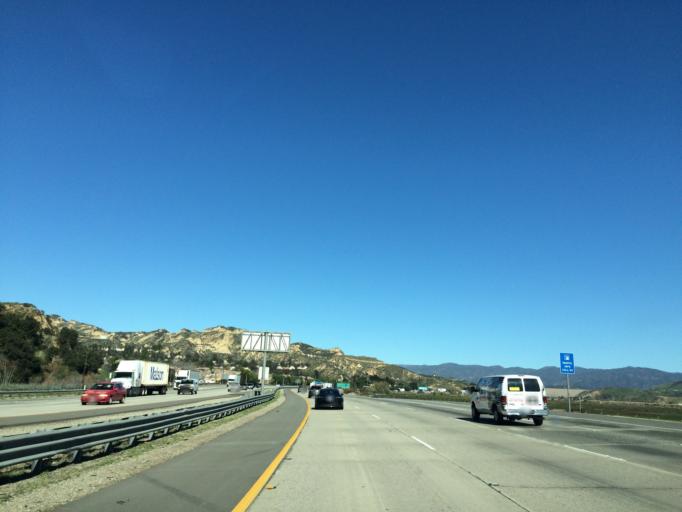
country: US
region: California
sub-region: Los Angeles County
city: Valencia
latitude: 34.4630
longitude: -118.6153
